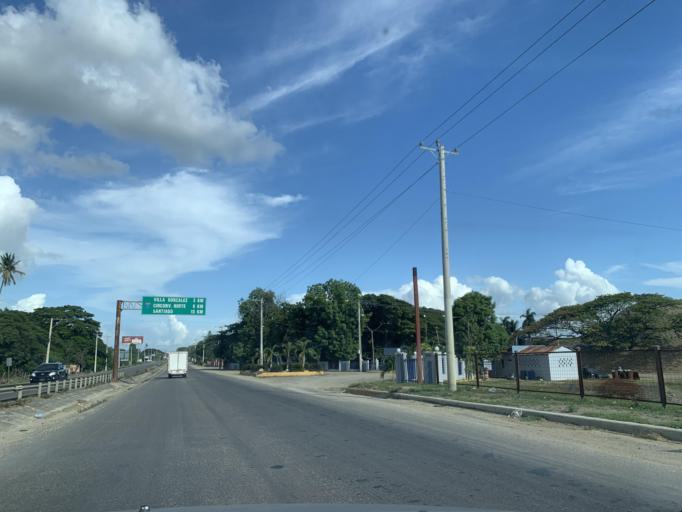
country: DO
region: Santiago
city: Villa Gonzalez
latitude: 19.5491
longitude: -70.8115
